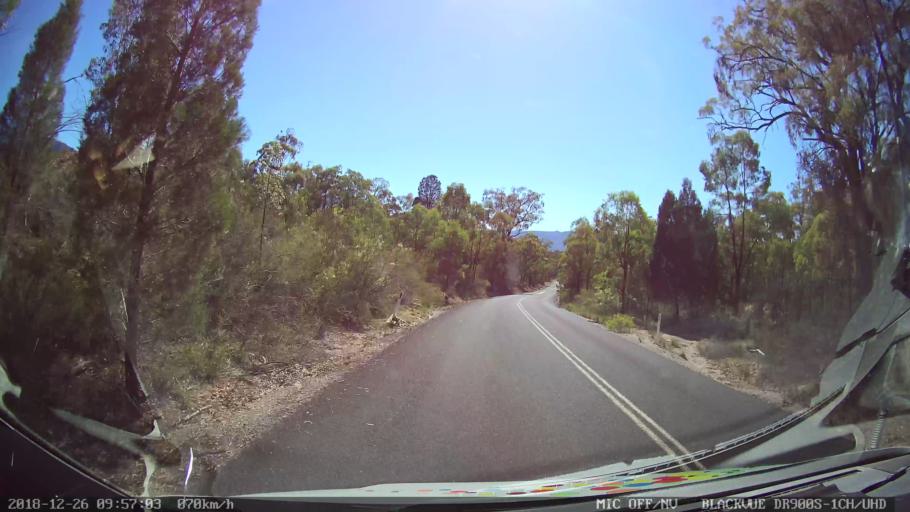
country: AU
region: New South Wales
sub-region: Mid-Western Regional
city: Kandos
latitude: -33.0397
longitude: 150.1874
